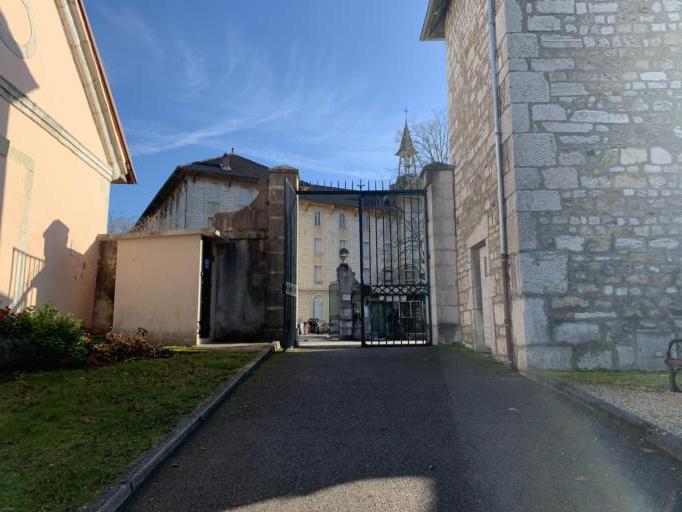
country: FR
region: Rhone-Alpes
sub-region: Departement de l'Ain
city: Belley
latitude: 45.7573
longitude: 5.6903
